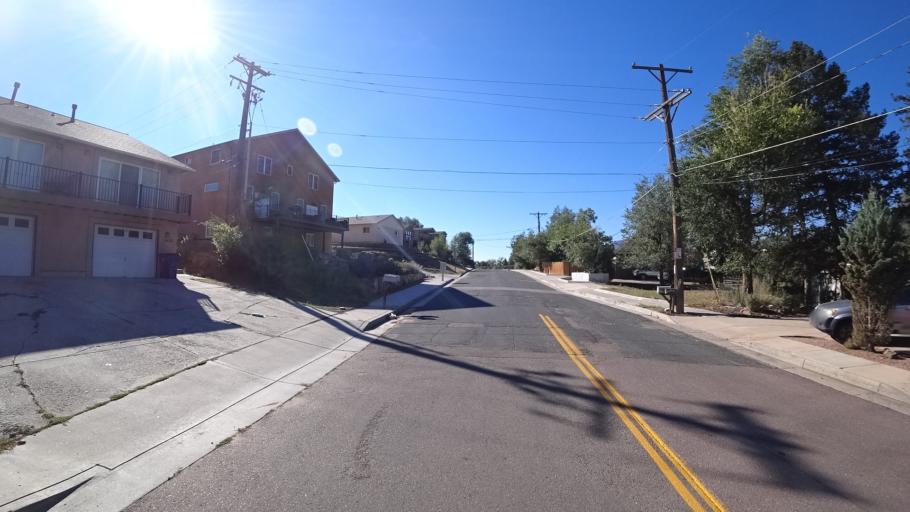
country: US
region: Colorado
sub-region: El Paso County
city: Colorado Springs
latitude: 38.8469
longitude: -104.8445
